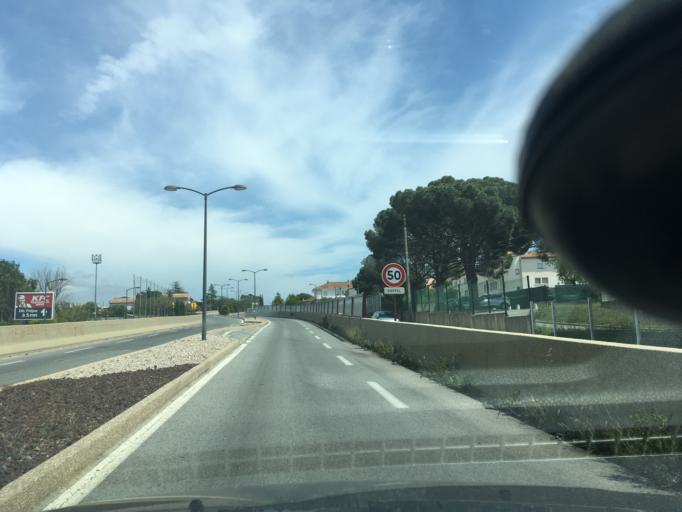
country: FR
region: Provence-Alpes-Cote d'Azur
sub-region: Departement du Var
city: Puget-sur-Argens
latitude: 43.4576
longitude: 6.6815
